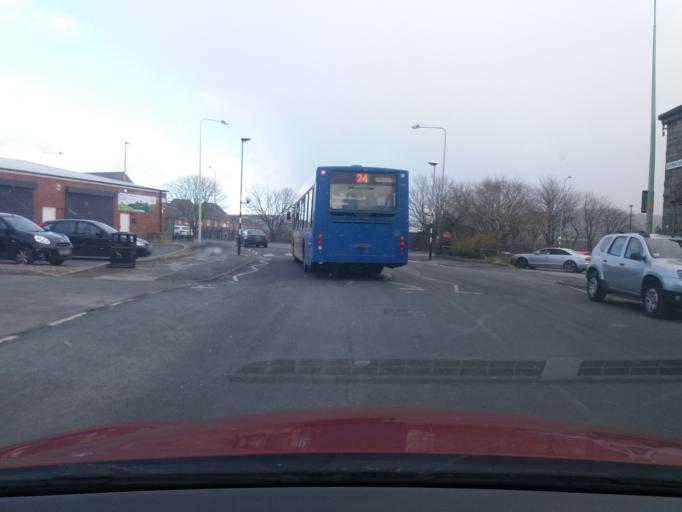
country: GB
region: England
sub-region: Lancashire
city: Chorley
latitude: 53.6615
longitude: -2.6196
